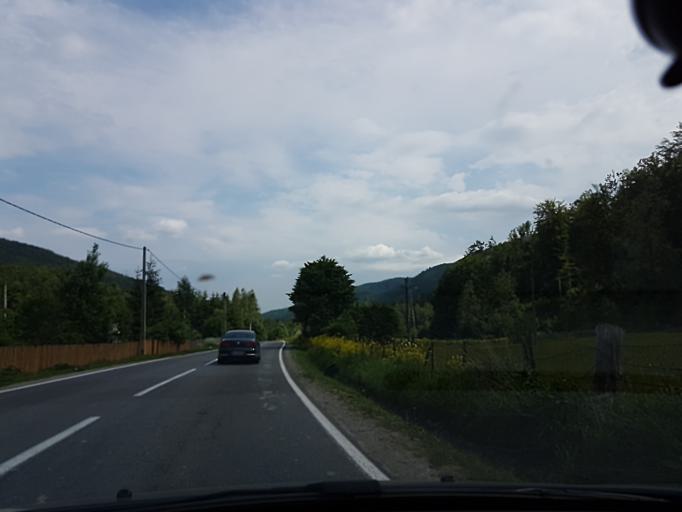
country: RO
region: Prahova
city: Maneciu
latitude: 45.3613
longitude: 25.9405
